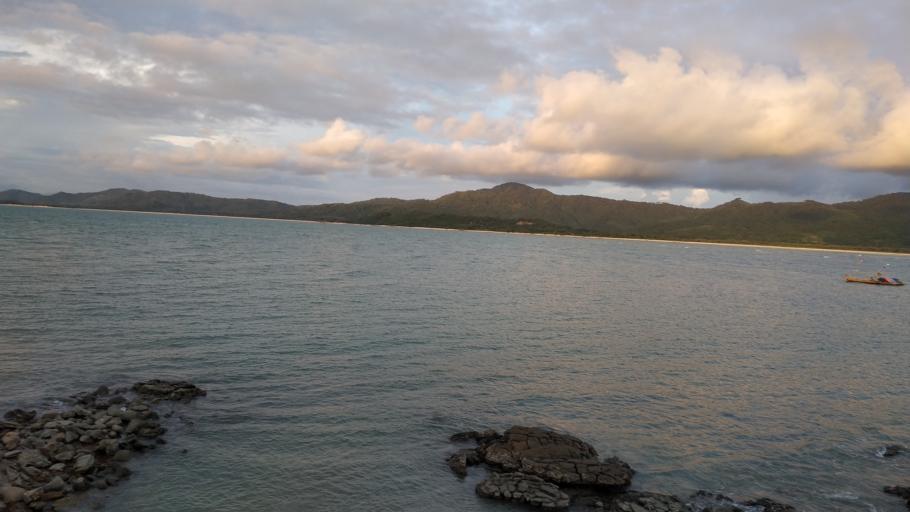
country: MM
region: Tanintharyi
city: Dawei
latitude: 14.0870
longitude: 98.0705
